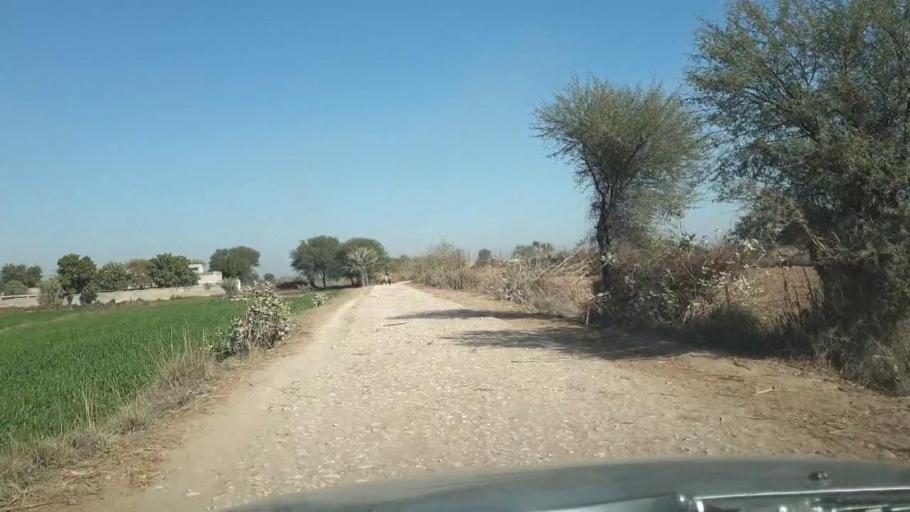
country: PK
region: Sindh
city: Ghotki
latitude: 28.0850
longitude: 69.3428
